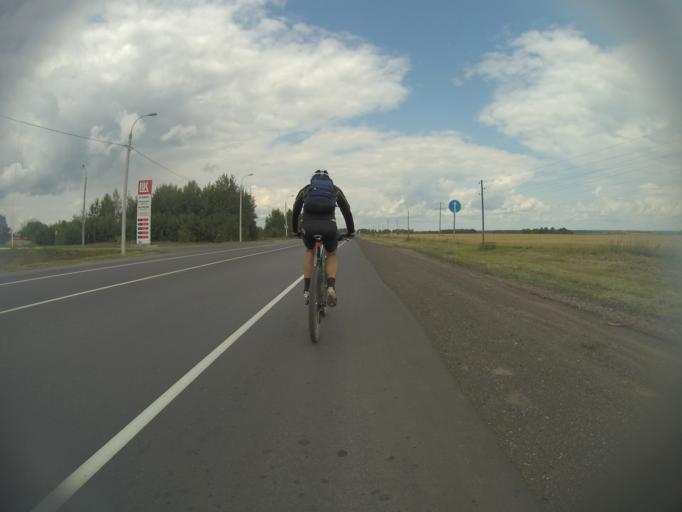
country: RU
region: Vladimir
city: Suzdal'
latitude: 56.4444
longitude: 40.4652
